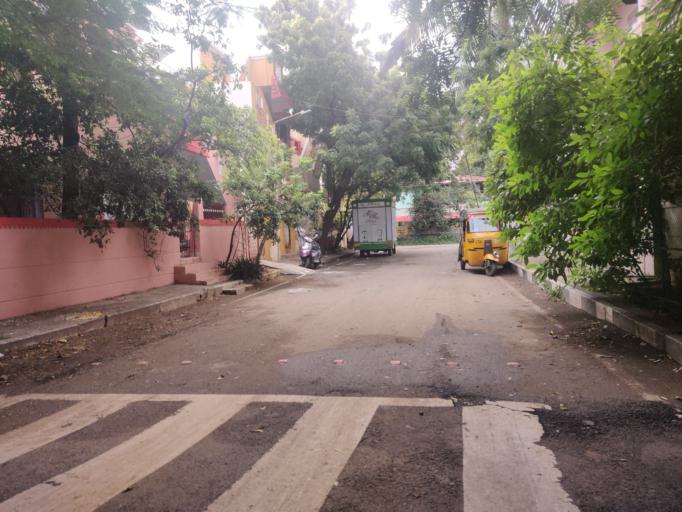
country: IN
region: Tamil Nadu
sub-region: Thiruvallur
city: Chinnasekkadu
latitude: 13.1230
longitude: 80.2196
